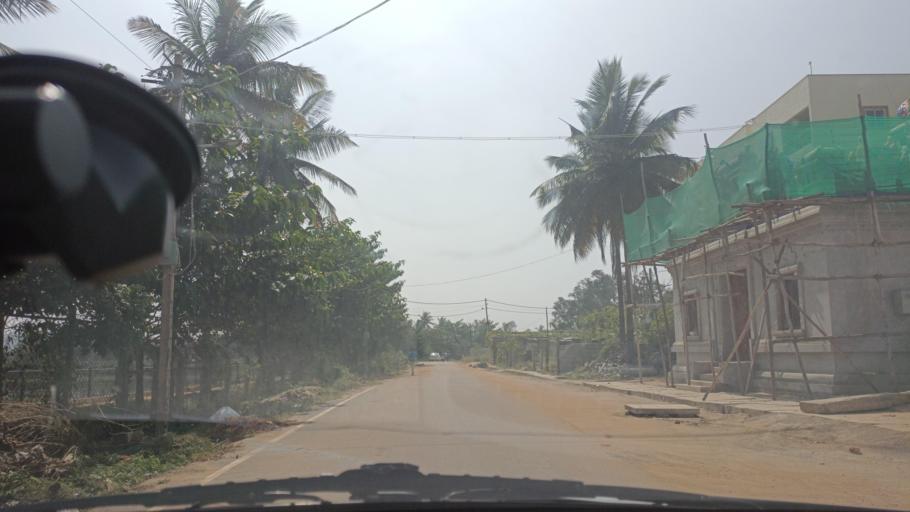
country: IN
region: Karnataka
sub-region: Bangalore Urban
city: Yelahanka
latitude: 13.1159
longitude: 77.6153
